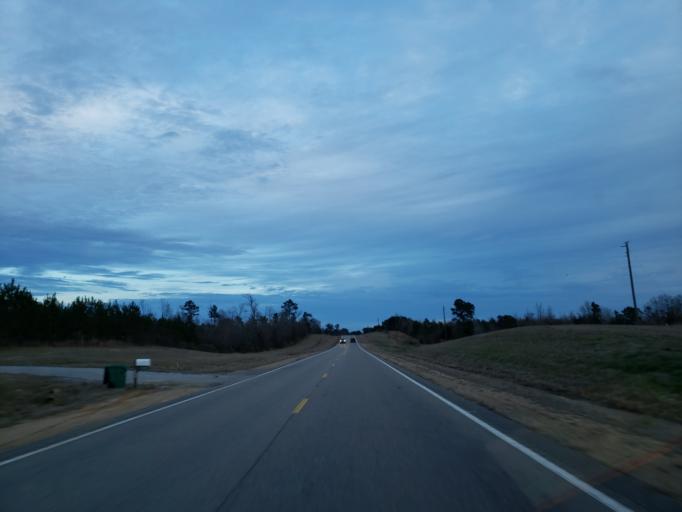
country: US
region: Mississippi
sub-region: Kemper County
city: De Kalb
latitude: 32.8308
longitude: -88.3760
